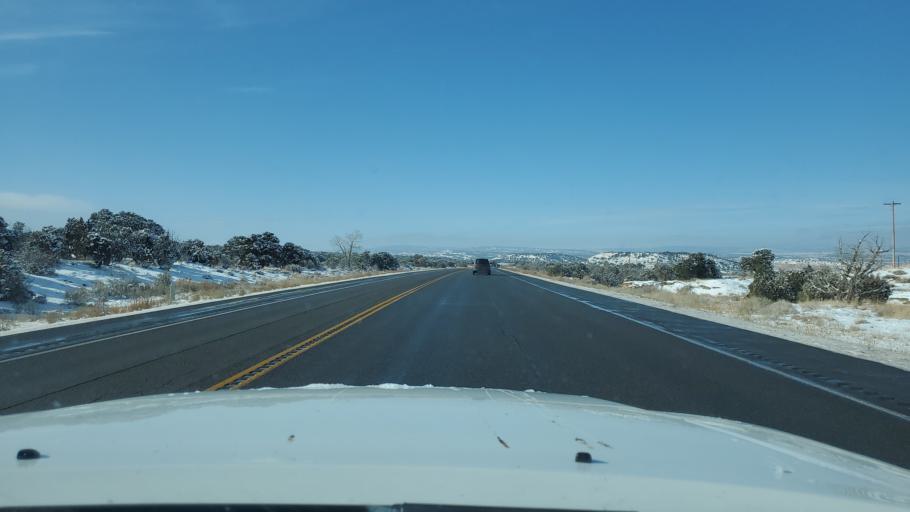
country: US
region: Utah
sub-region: Duchesne County
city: Duchesne
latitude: 40.1643
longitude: -110.4639
